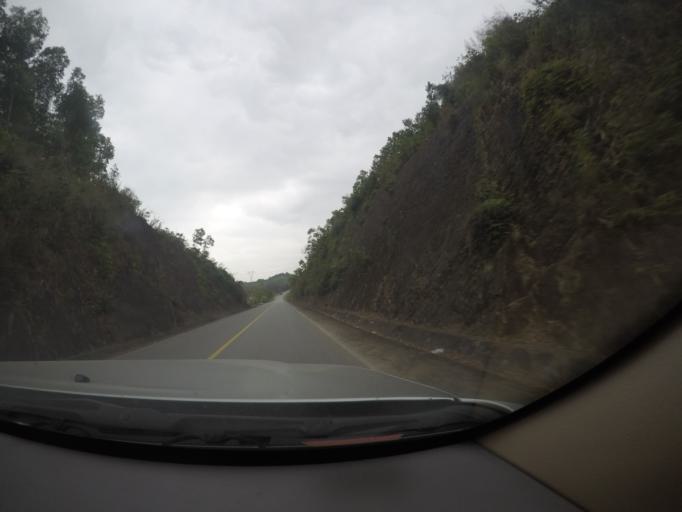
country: VN
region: Quang Binh
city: Hoan Lao
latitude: 17.6128
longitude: 106.4038
